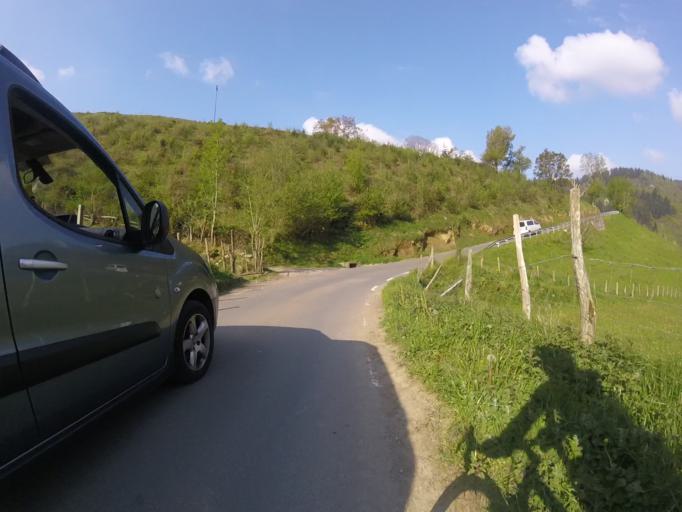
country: ES
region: Basque Country
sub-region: Provincia de Guipuzcoa
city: Azkoitia
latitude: 43.2295
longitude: -2.3186
